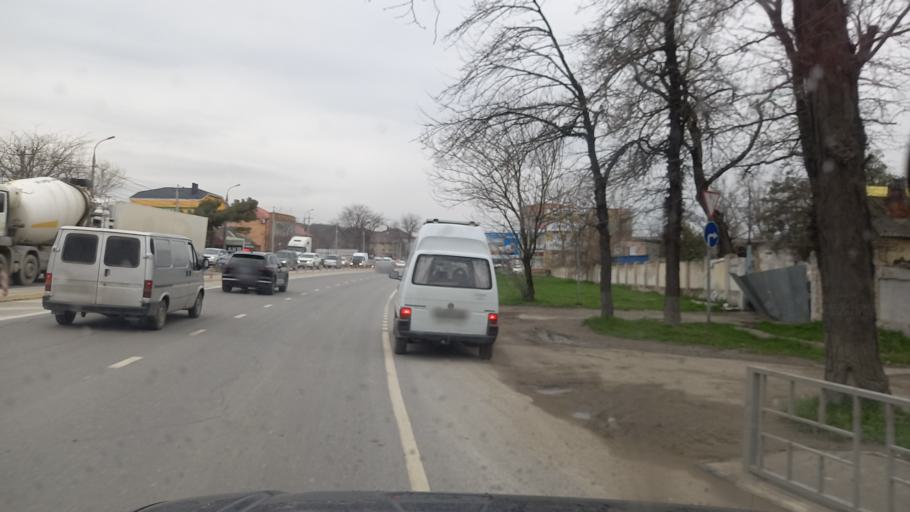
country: RU
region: Krasnodarskiy
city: Gayduk
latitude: 44.7689
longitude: 37.7000
